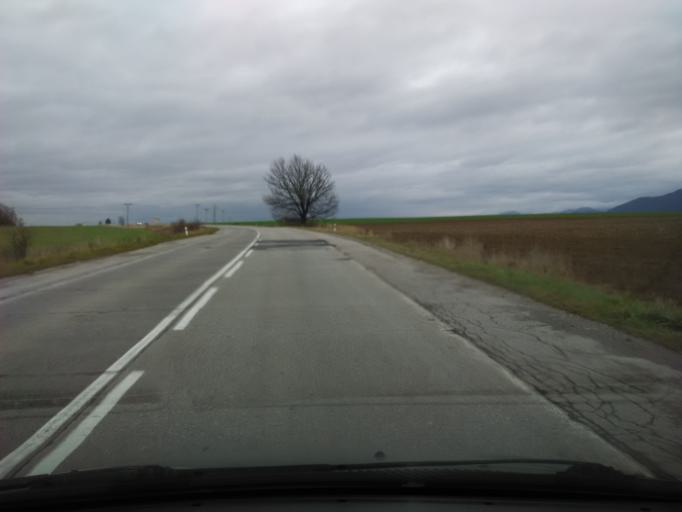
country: SK
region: Zilinsky
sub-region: Okres Martin
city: Martin
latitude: 48.9355
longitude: 18.8944
